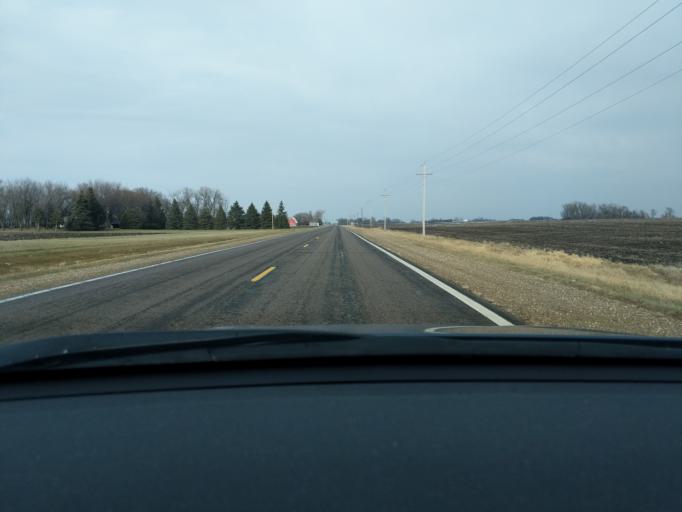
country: US
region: Minnesota
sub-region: Renville County
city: Renville
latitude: 44.7679
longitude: -95.3409
